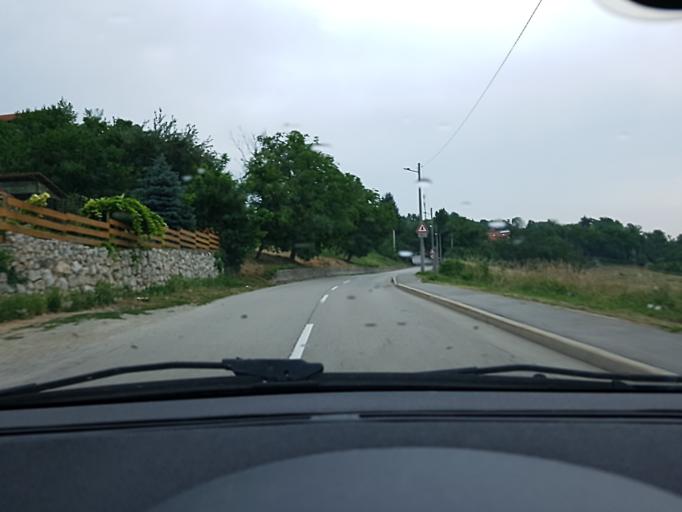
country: HR
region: Zagrebacka
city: Pojatno
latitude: 45.9222
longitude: 15.8080
